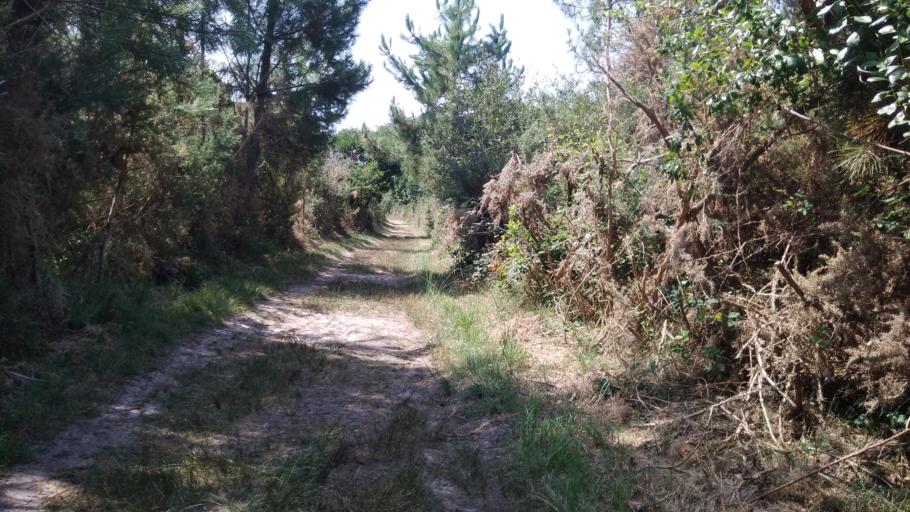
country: FR
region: Aquitaine
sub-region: Departement des Landes
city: Mimizan
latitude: 44.1963
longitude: -1.2968
